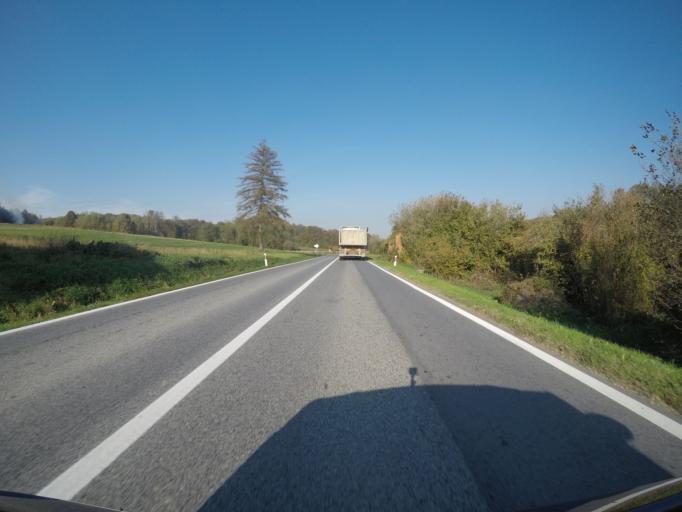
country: HR
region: Koprivnicko-Krizevacka
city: Virje
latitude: 46.0010
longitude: 16.9200
